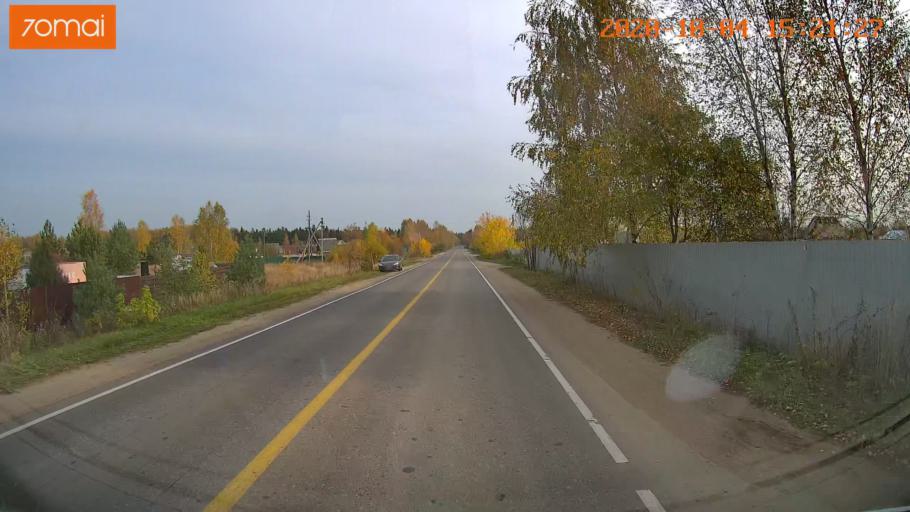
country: RU
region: Ivanovo
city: Bogorodskoye
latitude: 57.0863
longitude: 40.9229
